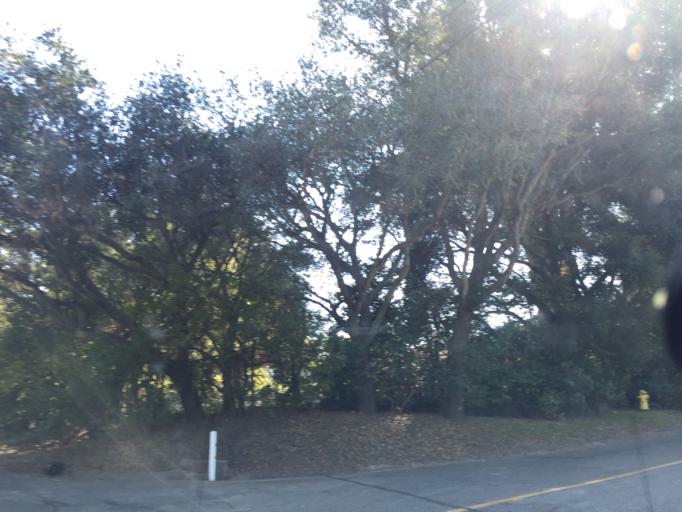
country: US
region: California
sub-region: Santa Barbara County
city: Mission Canyon
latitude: 34.4356
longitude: -119.7612
